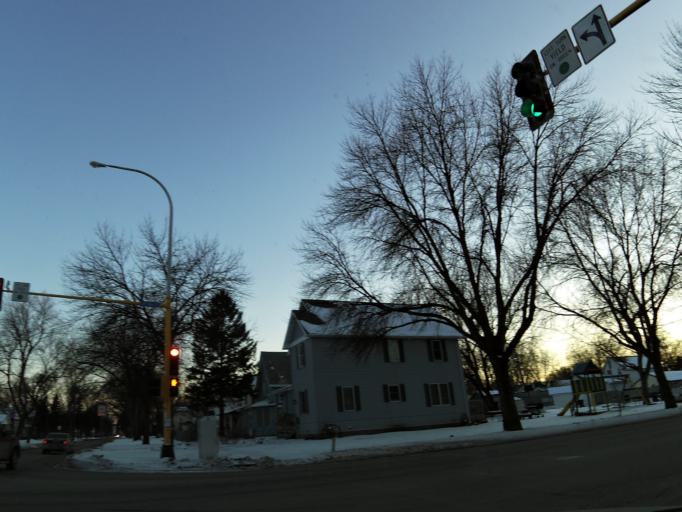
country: US
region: North Dakota
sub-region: Grand Forks County
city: Grand Forks
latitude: 47.9185
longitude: -97.0358
